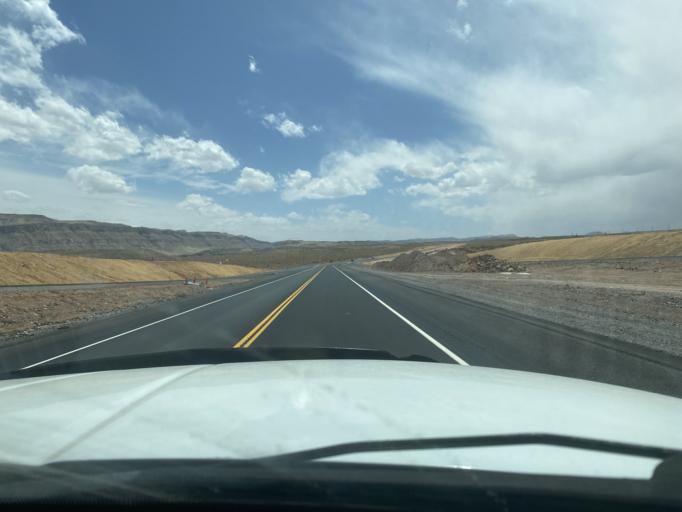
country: US
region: Utah
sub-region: Washington County
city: Hurricane
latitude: 37.1250
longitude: -113.3447
